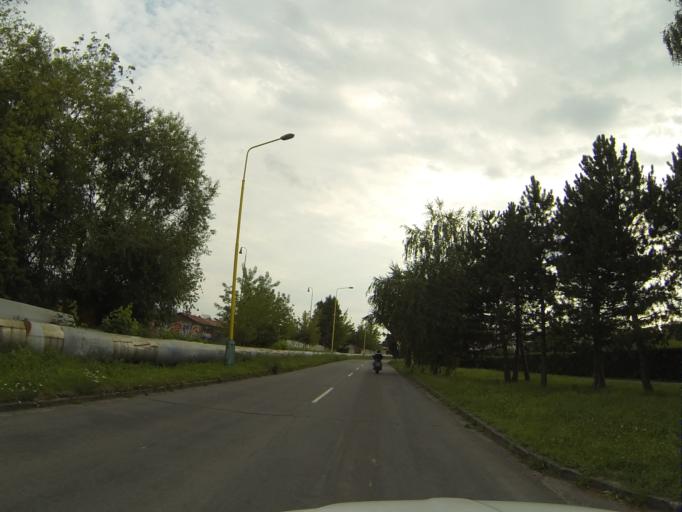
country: SK
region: Nitriansky
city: Prievidza
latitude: 48.7769
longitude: 18.6178
